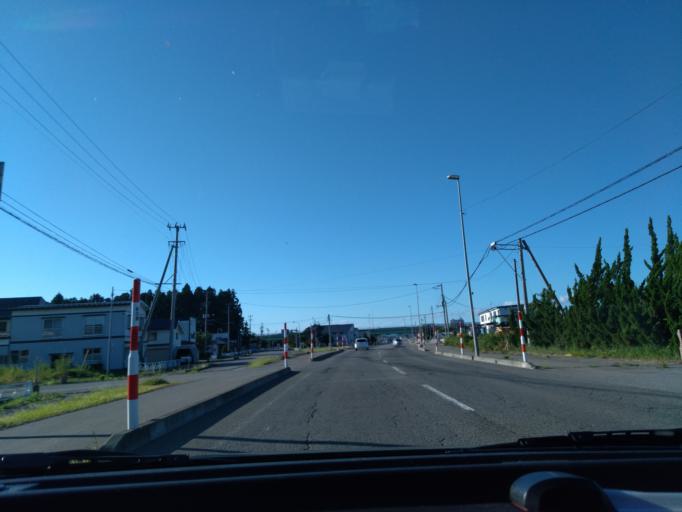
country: JP
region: Akita
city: Omagari
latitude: 39.4340
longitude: 140.4838
